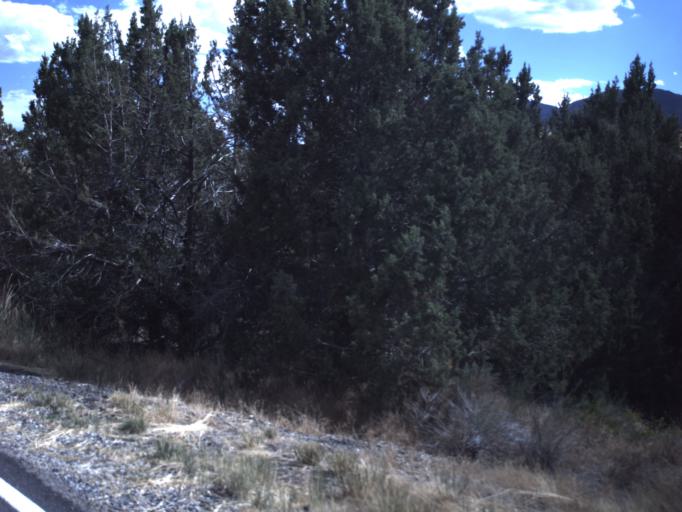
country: US
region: Utah
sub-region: Tooele County
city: Grantsville
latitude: 40.3389
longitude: -112.5354
